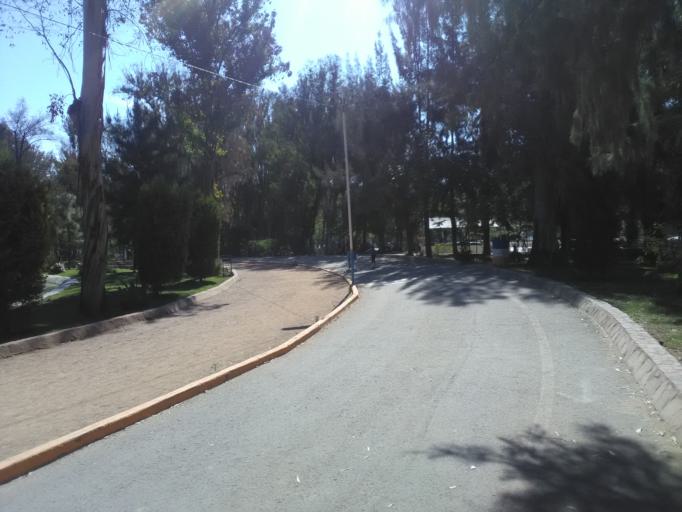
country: MX
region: Durango
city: Victoria de Durango
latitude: 24.0254
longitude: -104.6869
